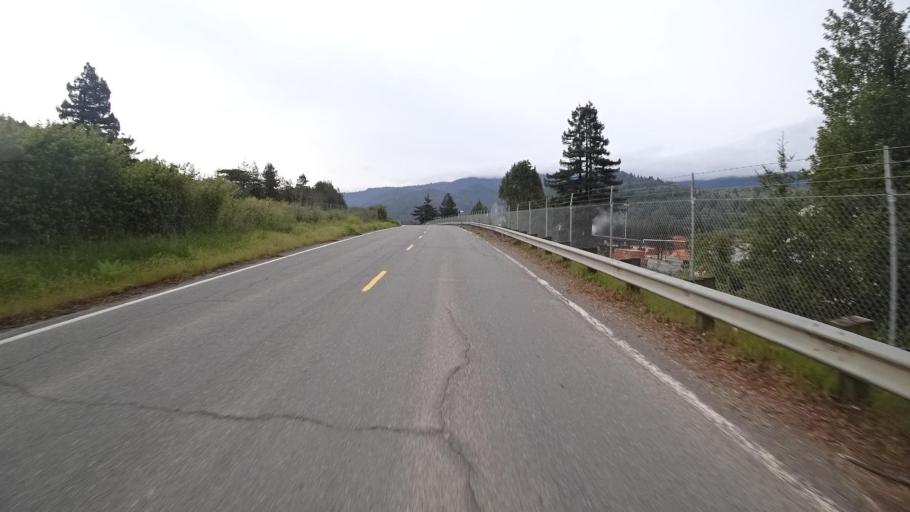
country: US
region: California
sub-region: Humboldt County
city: Rio Dell
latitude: 40.4739
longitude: -124.1003
